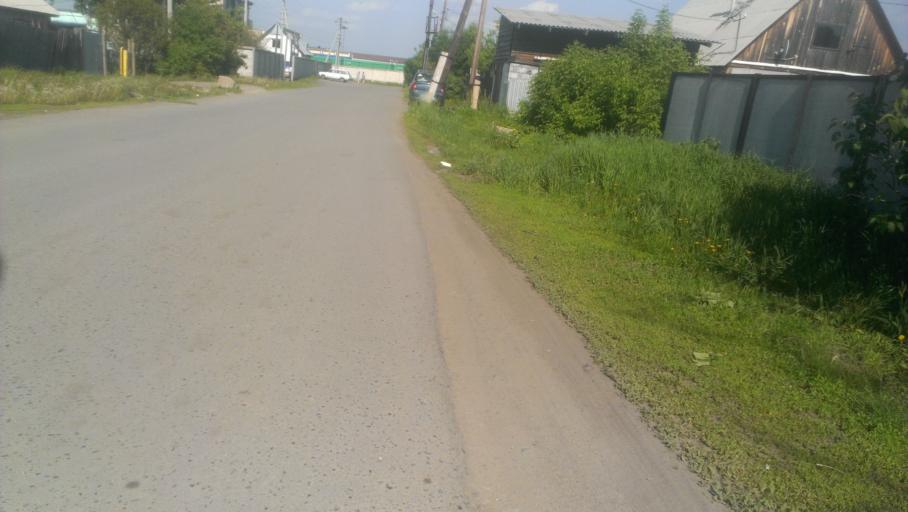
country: RU
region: Altai Krai
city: Novoaltaysk
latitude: 53.3975
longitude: 83.9364
